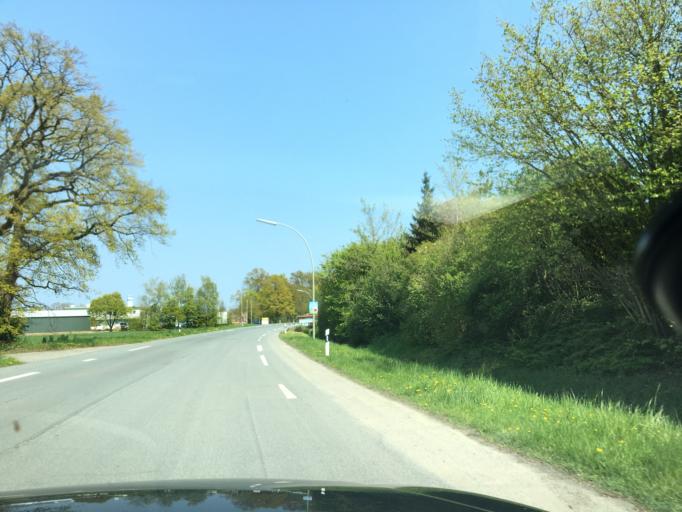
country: DE
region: North Rhine-Westphalia
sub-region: Regierungsbezirk Munster
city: Senden
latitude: 51.8453
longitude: 7.4728
